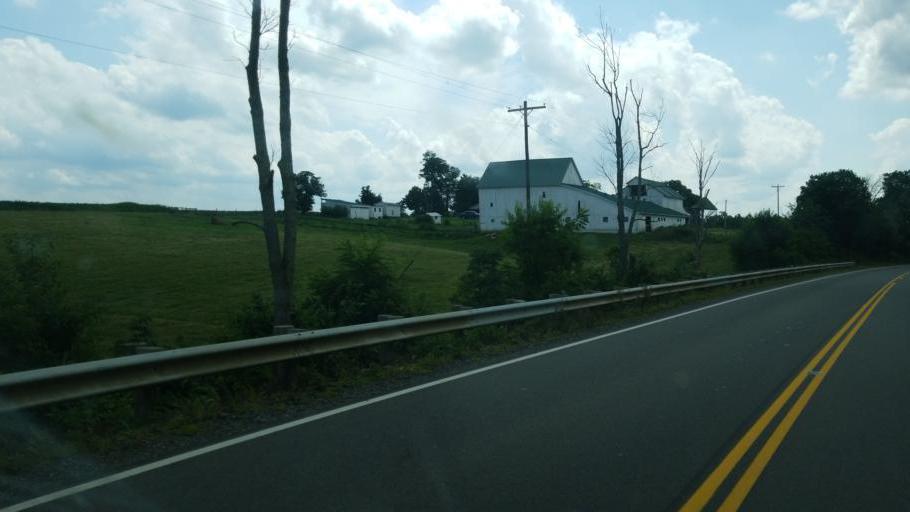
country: US
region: Ohio
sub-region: Knox County
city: Oak Hill
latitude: 40.3383
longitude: -82.1441
